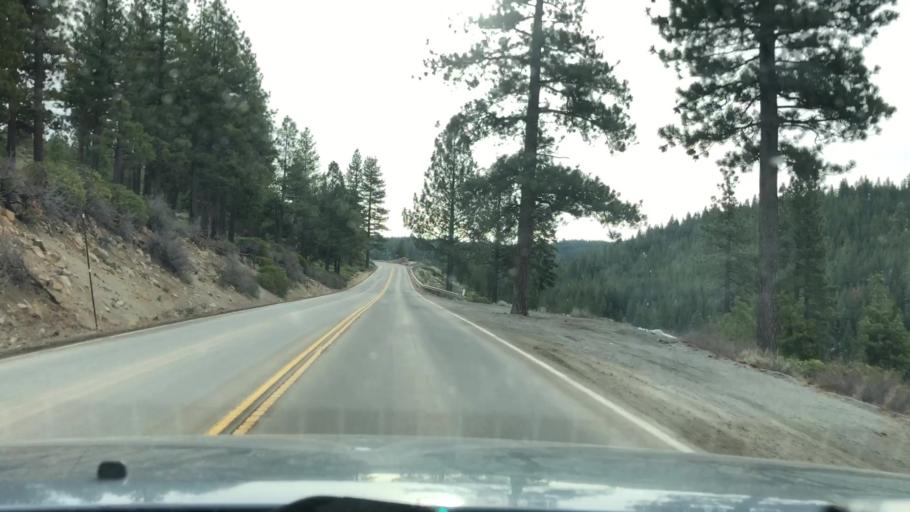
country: US
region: California
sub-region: Plumas County
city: Portola
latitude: 39.5594
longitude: -120.3487
